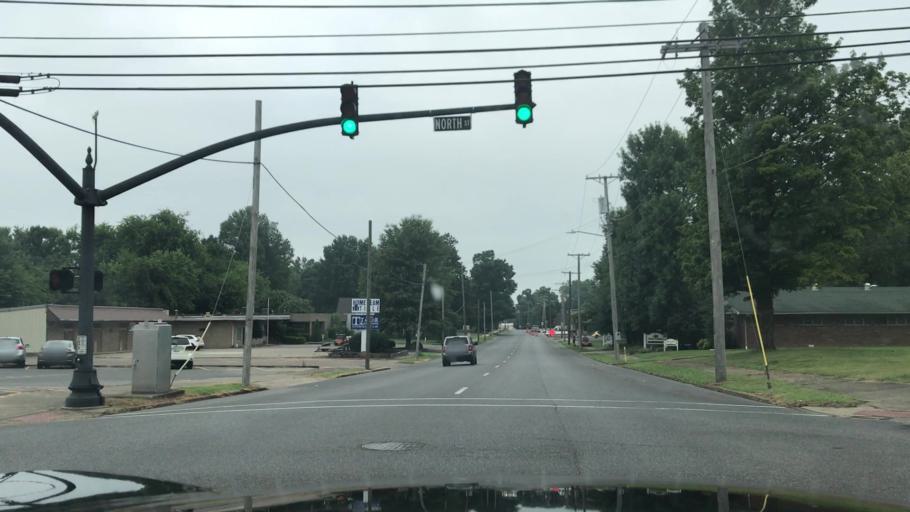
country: US
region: Kentucky
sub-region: Graves County
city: Mayfield
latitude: 36.7426
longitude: -88.6358
